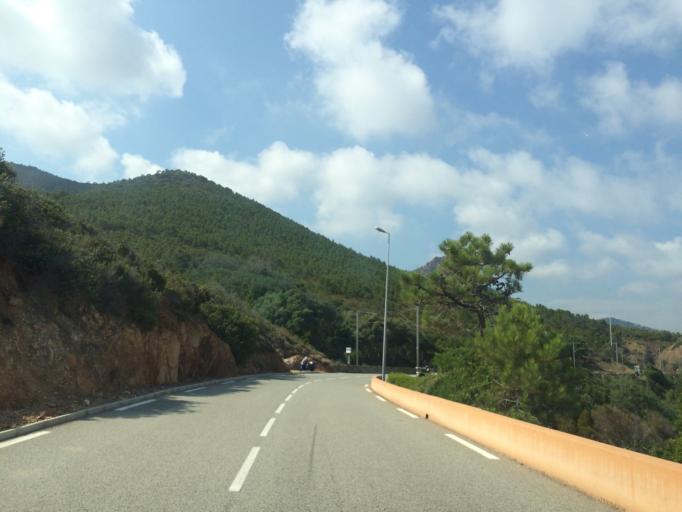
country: FR
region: Provence-Alpes-Cote d'Azur
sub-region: Departement des Alpes-Maritimes
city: Theoule-sur-Mer
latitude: 43.4520
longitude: 6.9201
